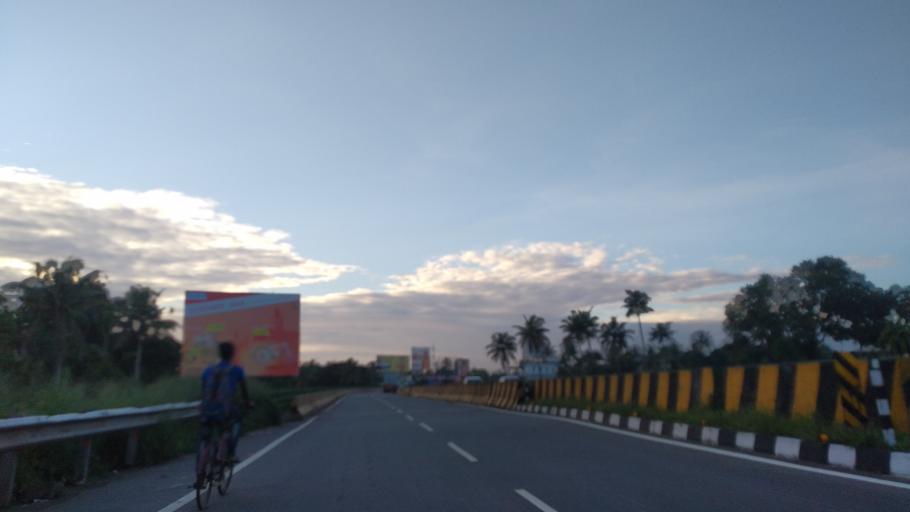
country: IN
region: Kerala
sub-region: Ernakulam
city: Elur
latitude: 10.0657
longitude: 76.3245
